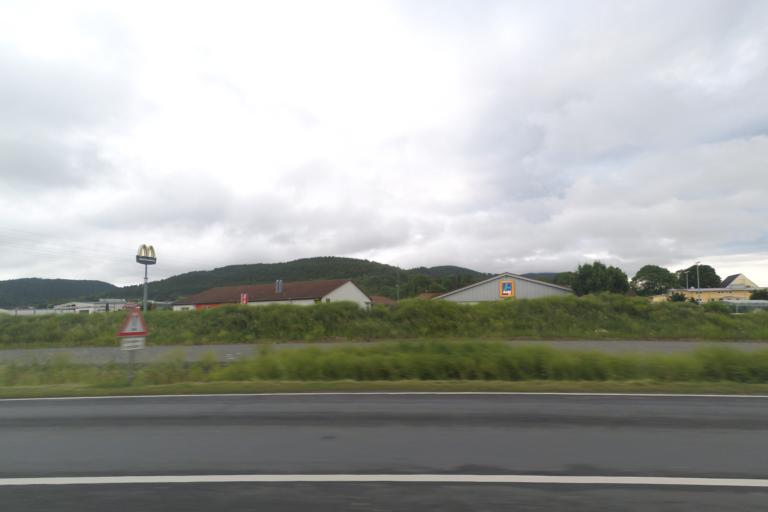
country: DE
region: Bavaria
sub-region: Upper Franconia
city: Marktrodach
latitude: 50.2567
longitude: 11.3957
